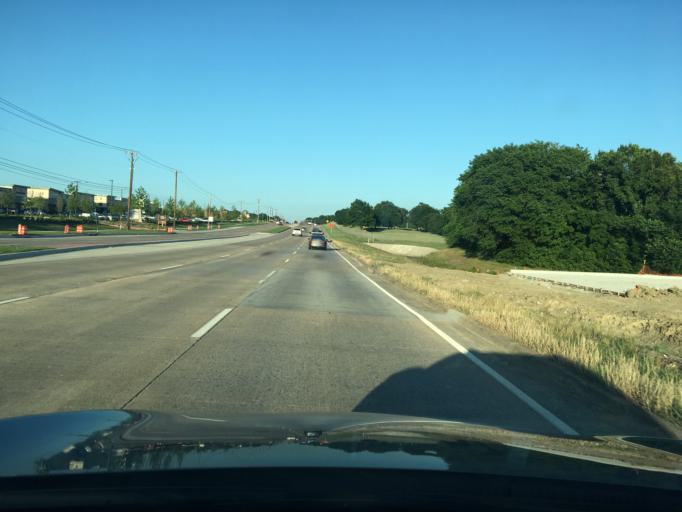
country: US
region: Texas
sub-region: Collin County
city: McKinney
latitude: 33.2172
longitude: -96.6596
